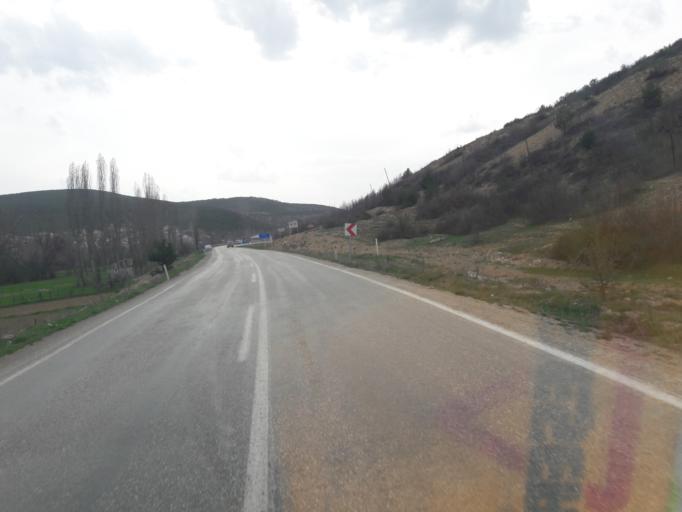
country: TR
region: Gumushane
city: Siran
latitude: 40.1769
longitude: 39.1401
